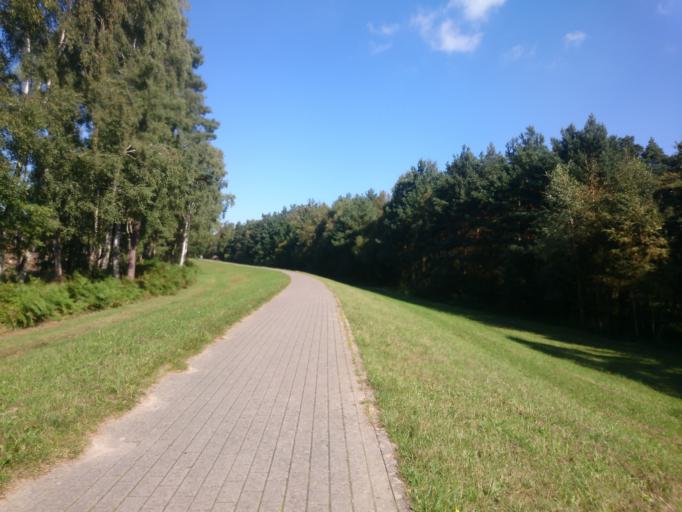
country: DE
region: Mecklenburg-Vorpommern
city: Zingst
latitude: 54.4330
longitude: 12.6637
